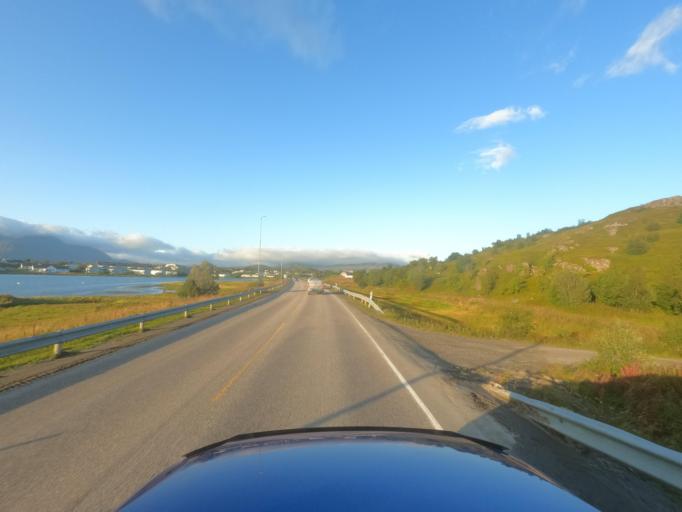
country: NO
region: Nordland
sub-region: Vestvagoy
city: Leknes
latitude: 68.1391
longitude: 13.5963
